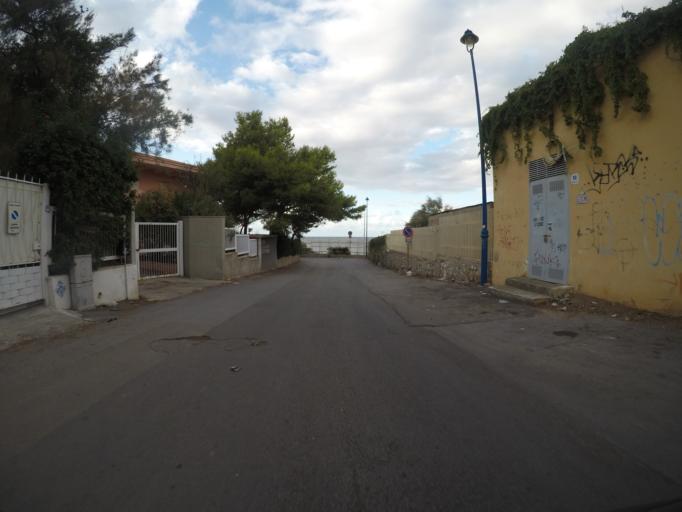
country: IT
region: Sicily
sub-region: Palermo
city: Palermo
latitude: 38.2110
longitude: 13.3277
